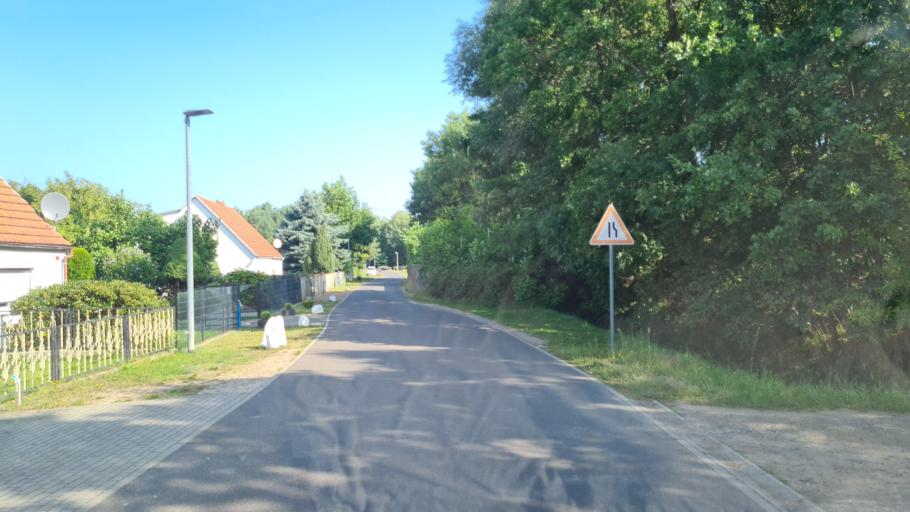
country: DE
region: Brandenburg
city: Kolkwitz
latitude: 51.7140
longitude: 14.2695
